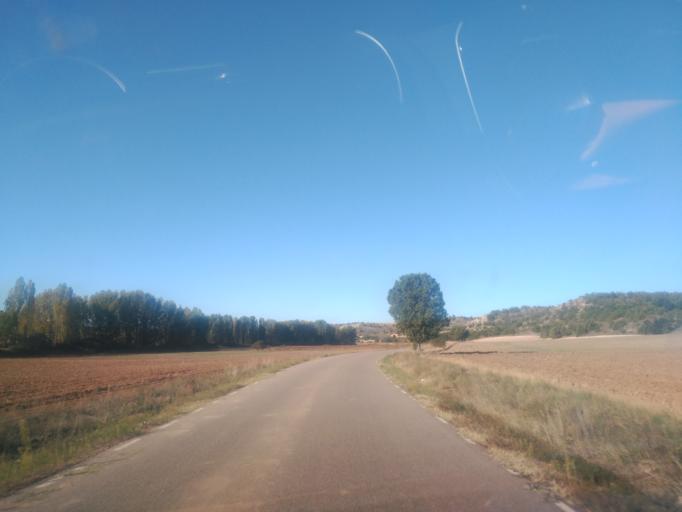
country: ES
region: Castille and Leon
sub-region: Provincia de Burgos
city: Arandilla
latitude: 41.6906
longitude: -3.4107
